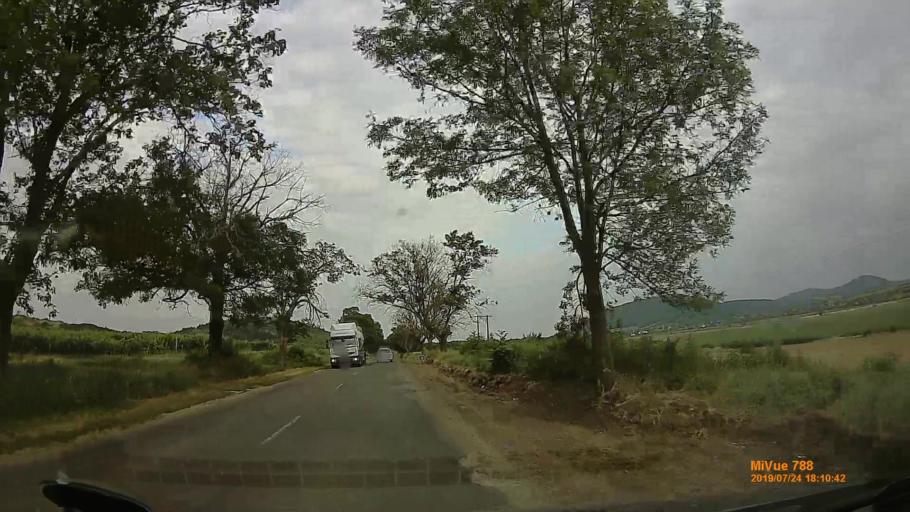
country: HU
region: Borsod-Abauj-Zemplen
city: Abaujszanto
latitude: 48.2572
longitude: 21.1916
